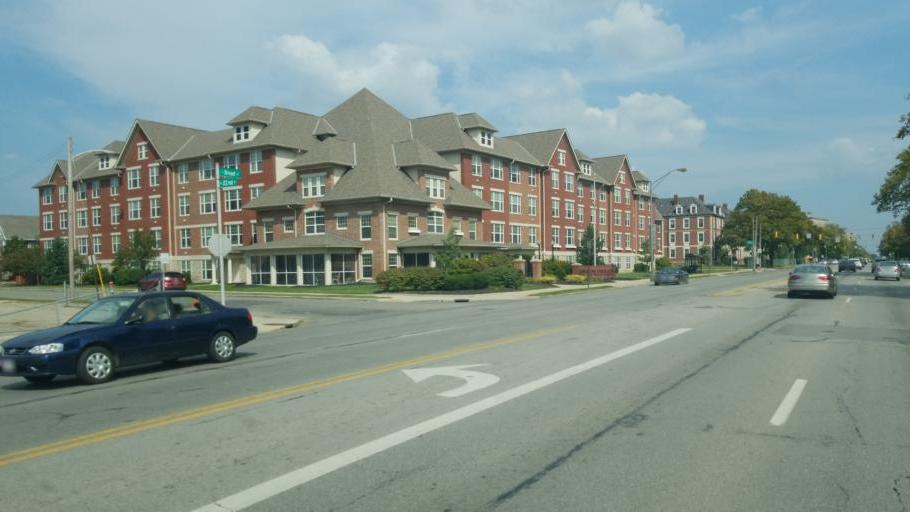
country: US
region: Ohio
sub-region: Franklin County
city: Columbus
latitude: 39.9655
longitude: -82.9717
